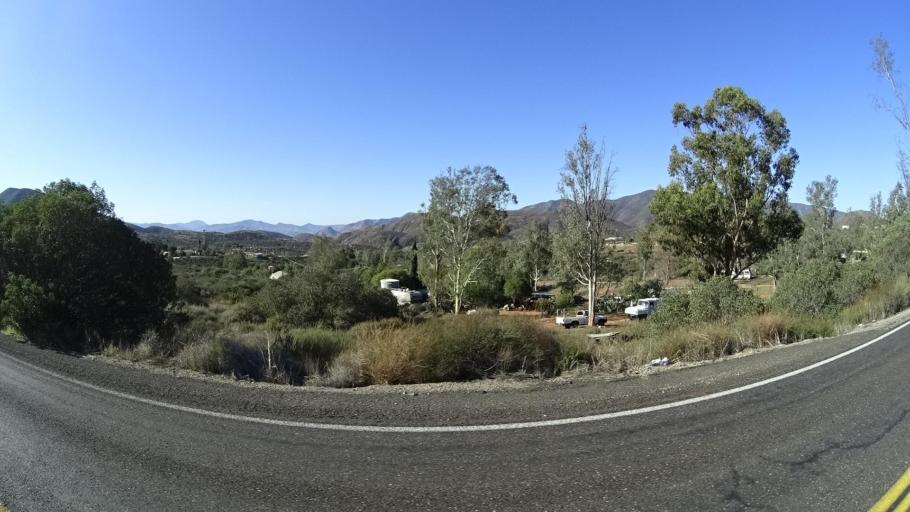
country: MX
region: Baja California
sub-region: Tijuana
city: Villa del Campo
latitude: 32.6202
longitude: -116.7432
